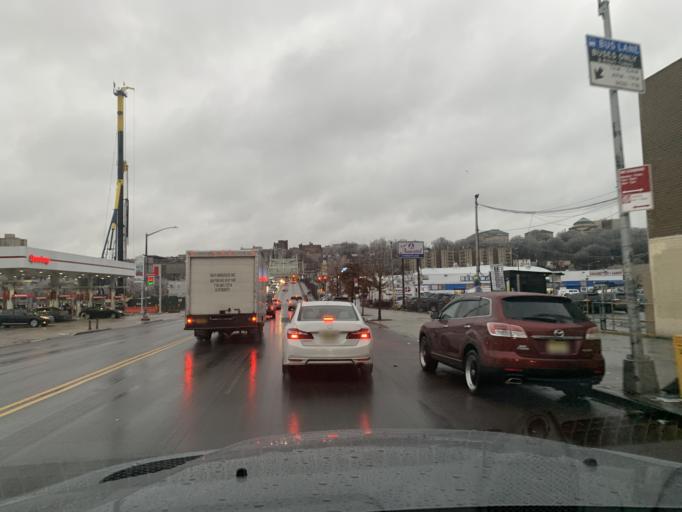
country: US
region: New York
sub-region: New York County
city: Inwood
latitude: 40.8641
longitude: -73.9181
